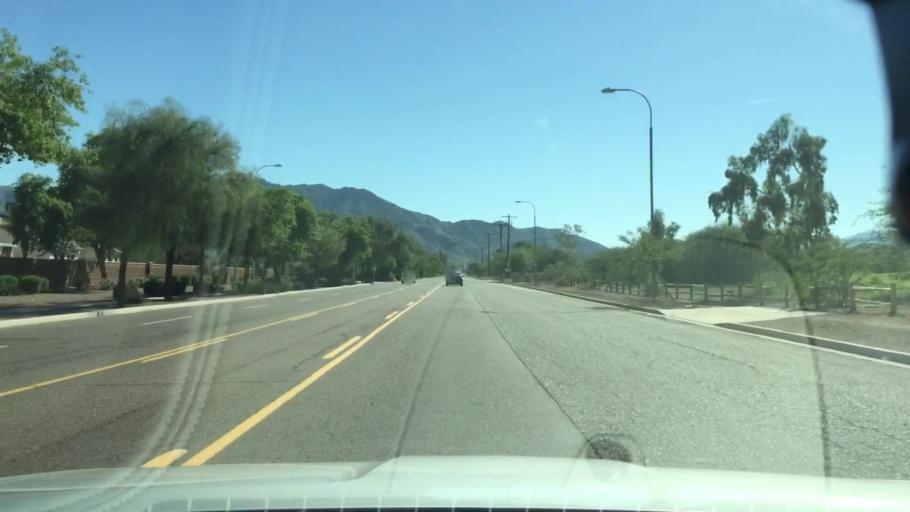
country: US
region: Arizona
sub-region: Maricopa County
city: Laveen
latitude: 33.3718
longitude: -112.1348
